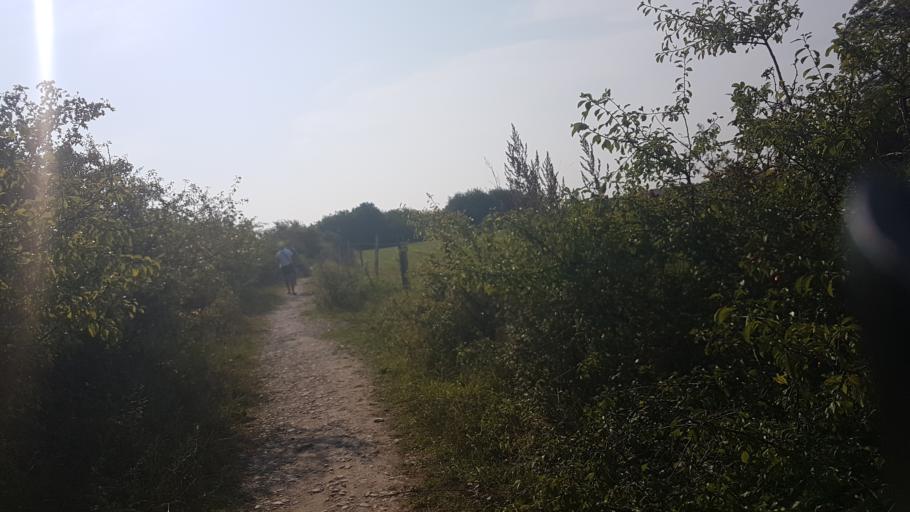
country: DE
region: Mecklenburg-Vorpommern
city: Putbus
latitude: 54.3099
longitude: 13.4357
